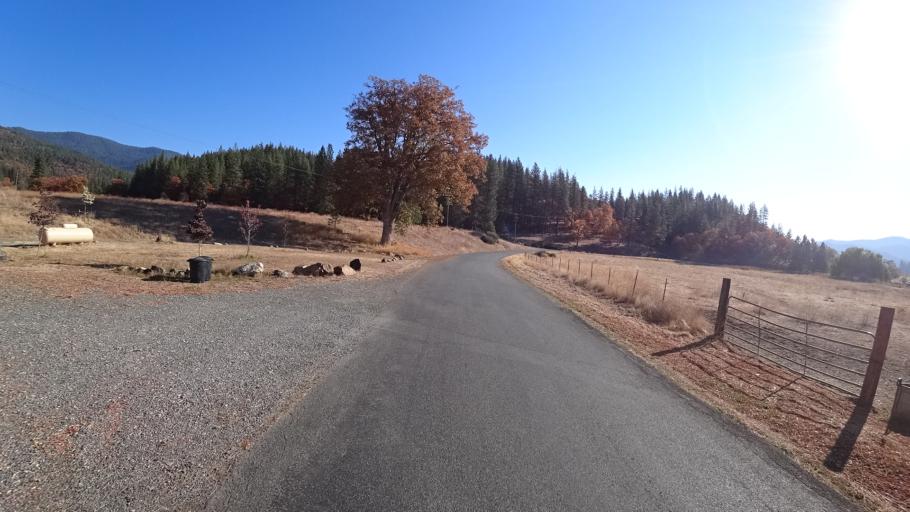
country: US
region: California
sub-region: Siskiyou County
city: Yreka
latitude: 41.6406
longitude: -122.9899
